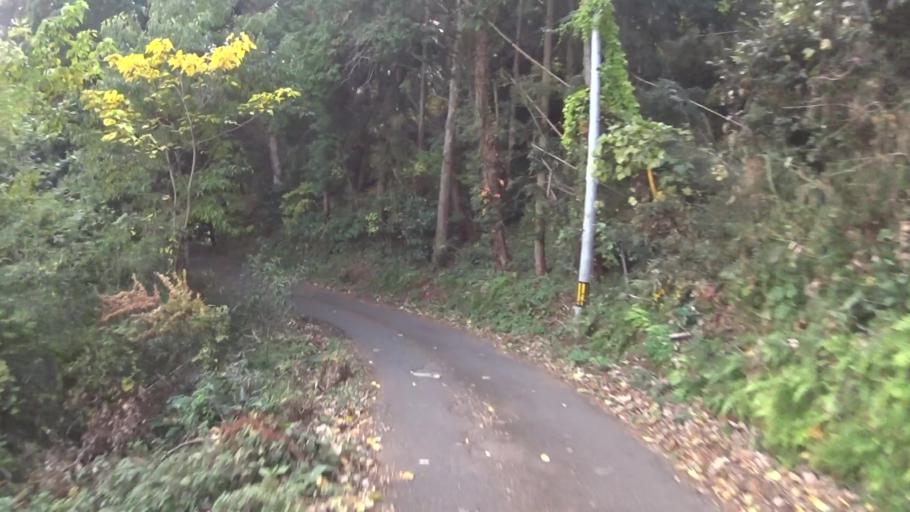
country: JP
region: Kyoto
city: Maizuru
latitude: 35.5640
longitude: 135.4634
